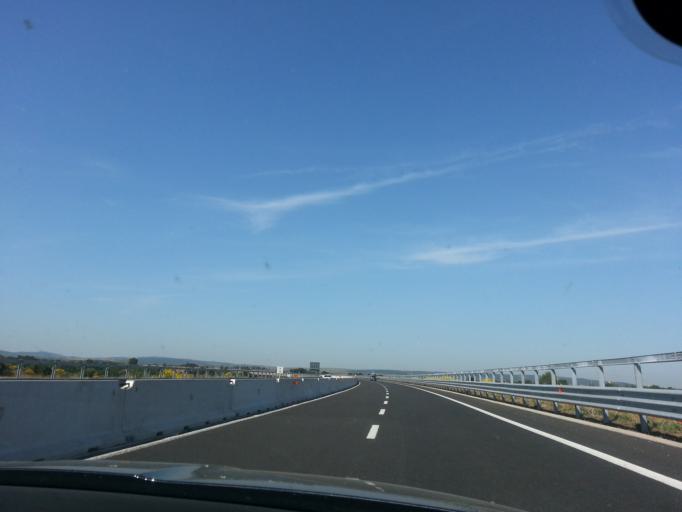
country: IT
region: Latium
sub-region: Provincia di Viterbo
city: Vetralla
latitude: 42.3613
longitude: 11.9915
